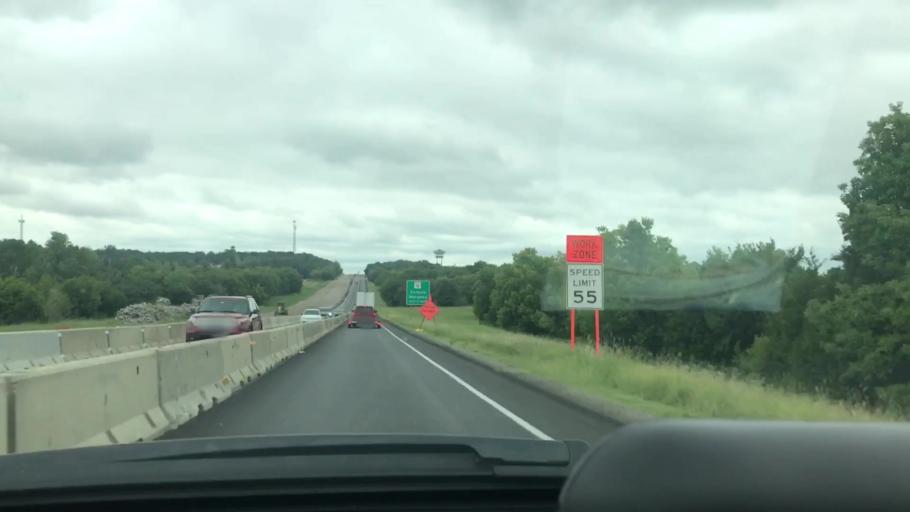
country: US
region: Oklahoma
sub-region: McIntosh County
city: Eufaula
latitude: 35.2772
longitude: -95.5931
